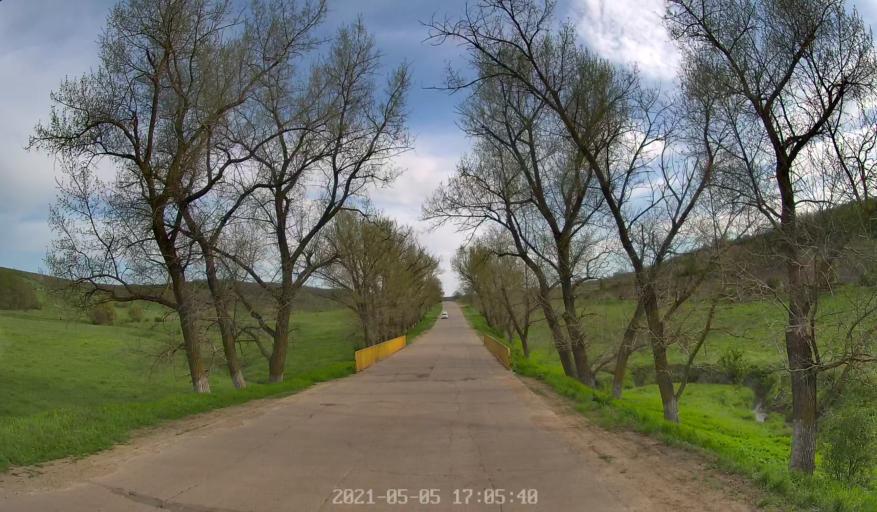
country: MD
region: Chisinau
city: Vadul lui Voda
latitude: 47.0277
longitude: 29.1391
